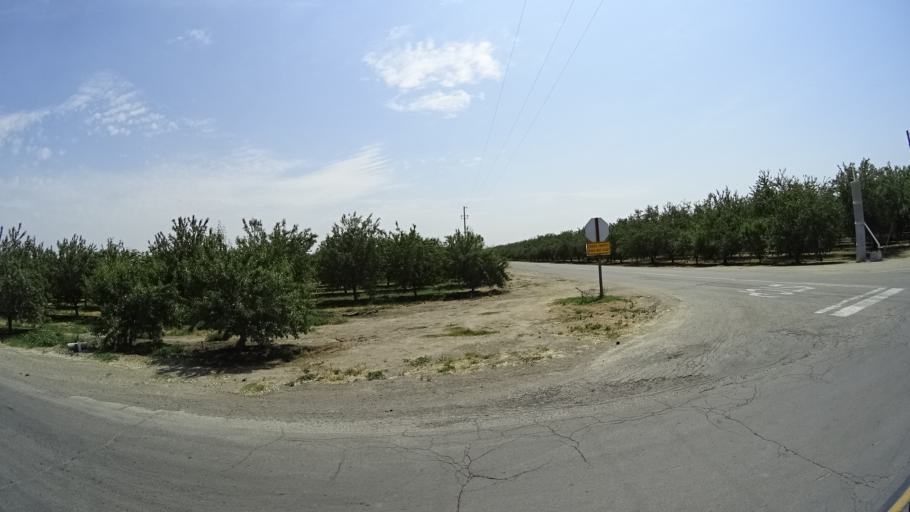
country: US
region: California
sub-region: Kings County
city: Armona
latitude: 36.3720
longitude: -119.7450
